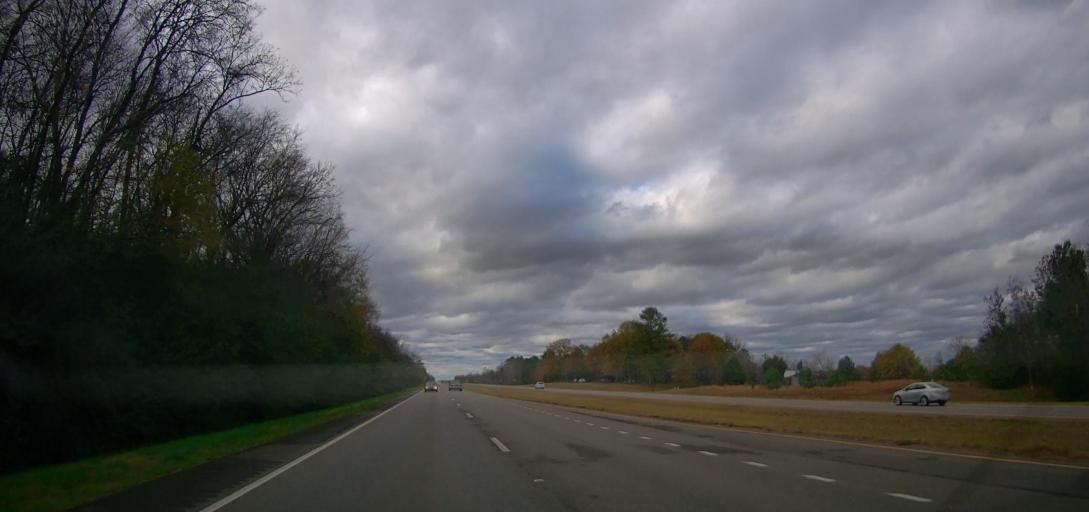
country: US
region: Alabama
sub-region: Morgan County
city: Falkville
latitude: 34.3304
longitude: -87.0085
